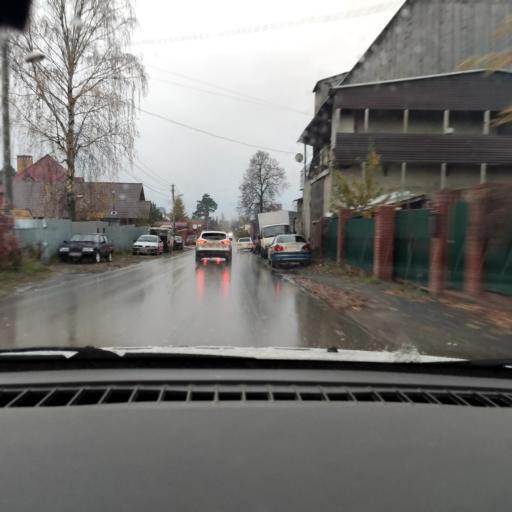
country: RU
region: Perm
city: Kondratovo
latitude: 58.0477
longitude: 56.1203
